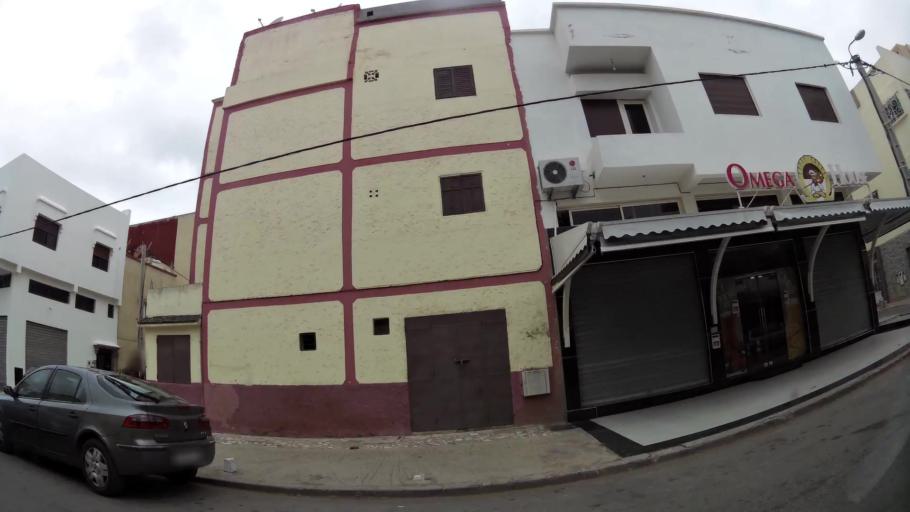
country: MA
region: Rabat-Sale-Zemmour-Zaer
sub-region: Rabat
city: Rabat
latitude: 33.9700
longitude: -6.8209
